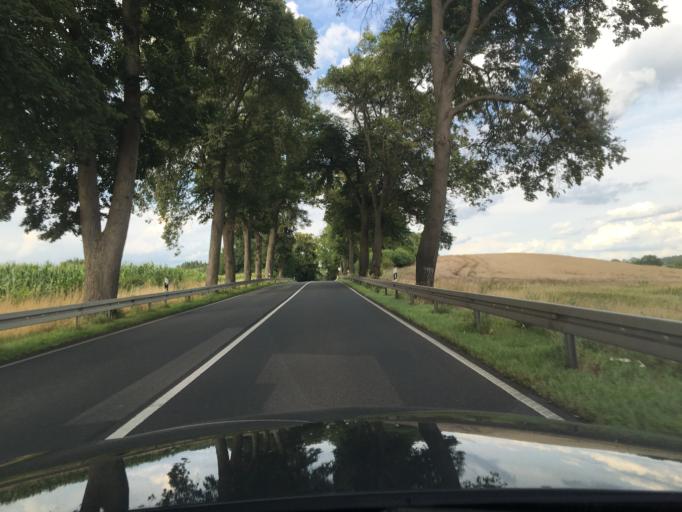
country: DE
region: Mecklenburg-Vorpommern
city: Wustrow
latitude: 53.4152
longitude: 13.1302
